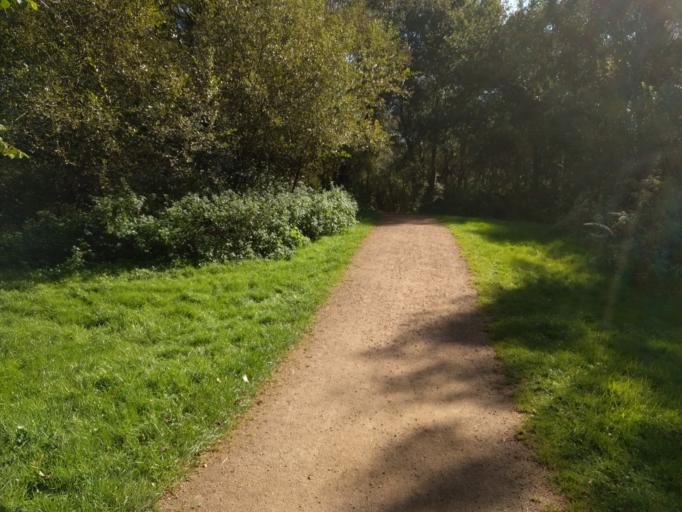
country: GB
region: England
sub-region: Warrington
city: Culcheth
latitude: 53.4205
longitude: -2.5082
